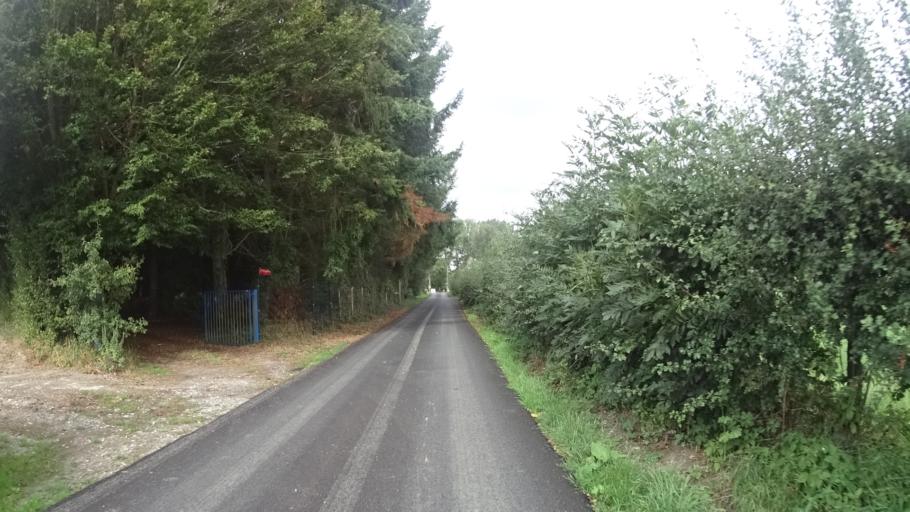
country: FR
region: Picardie
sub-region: Departement de l'Aisne
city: Wassigny
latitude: 50.0458
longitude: 3.6472
